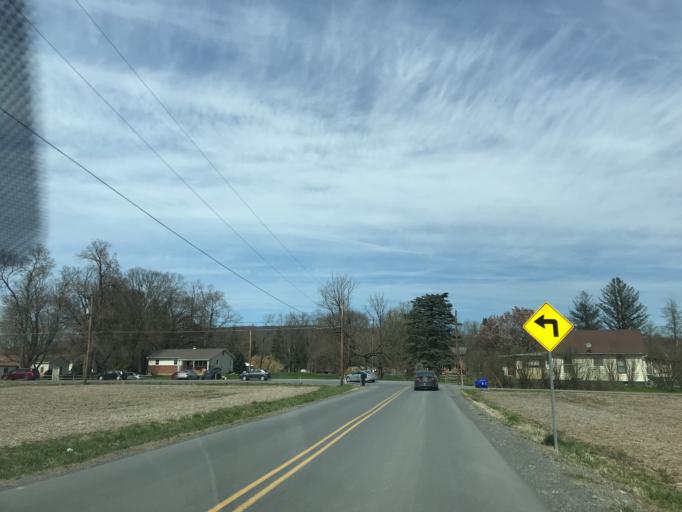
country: US
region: Pennsylvania
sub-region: Northumberland County
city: Northumberland
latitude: 40.9070
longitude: -76.8485
